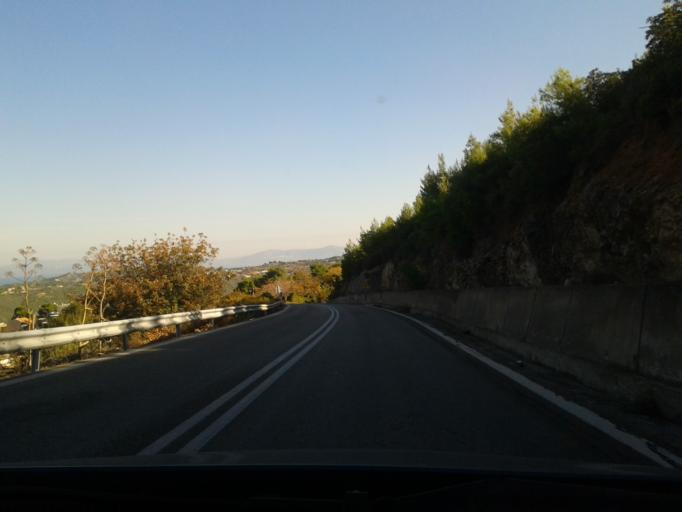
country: GR
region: Attica
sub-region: Nomarchia Anatolikis Attikis
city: Markopoulo Oropou
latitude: 38.2785
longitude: 23.7912
